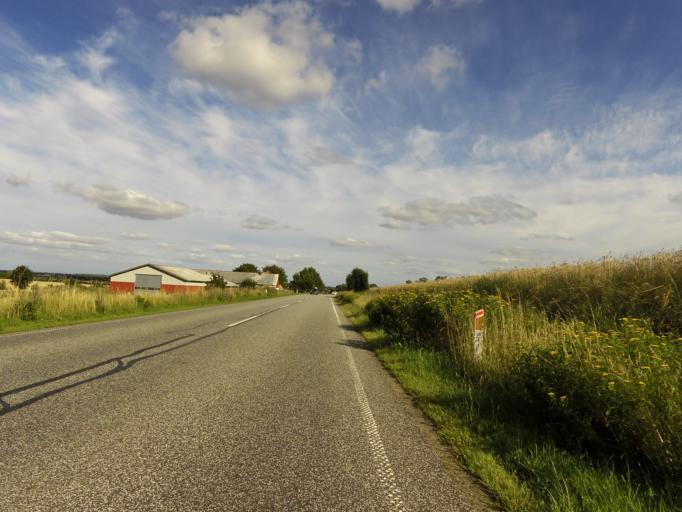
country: DK
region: South Denmark
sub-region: Haderslev Kommune
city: Gram
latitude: 55.2270
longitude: 8.9976
